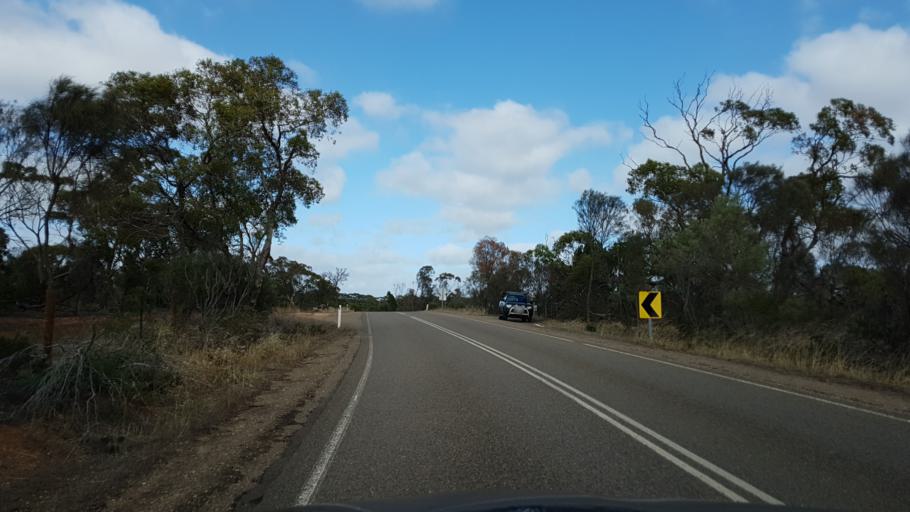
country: AU
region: South Australia
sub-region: Murray Bridge
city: Murray Bridge
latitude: -35.1123
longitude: 139.2223
